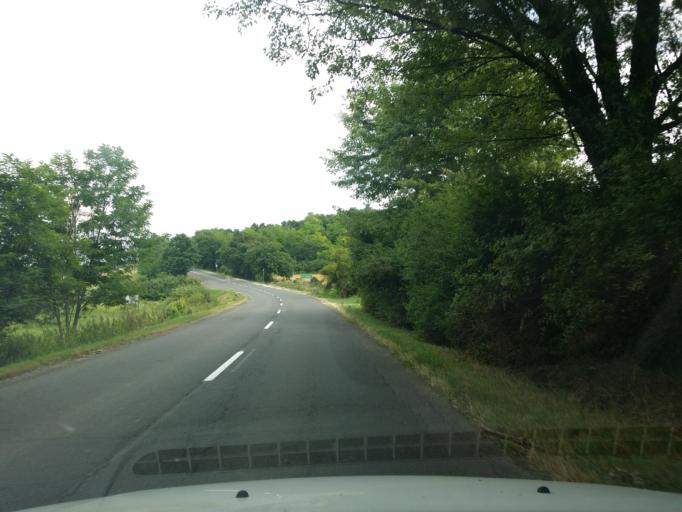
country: HU
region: Nograd
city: Bercel
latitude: 47.9425
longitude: 19.3681
